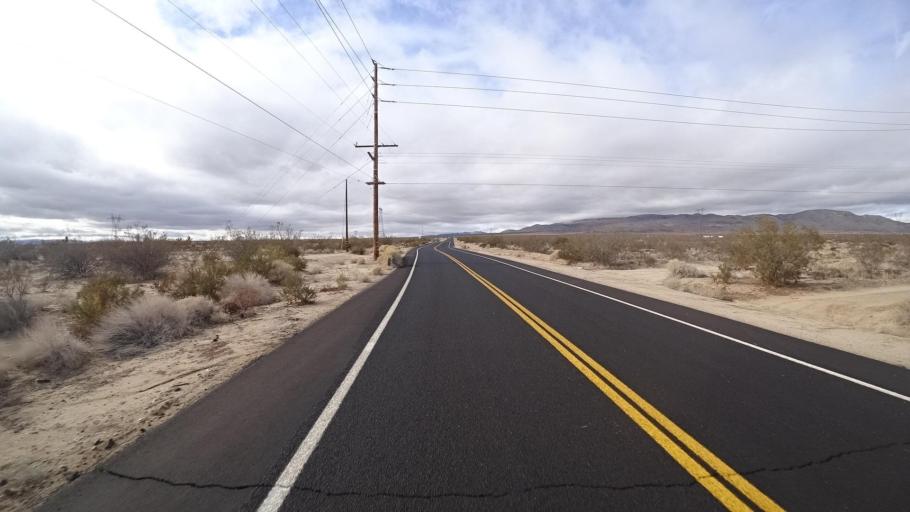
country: US
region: California
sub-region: Kern County
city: Mojave
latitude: 34.9509
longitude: -118.3096
